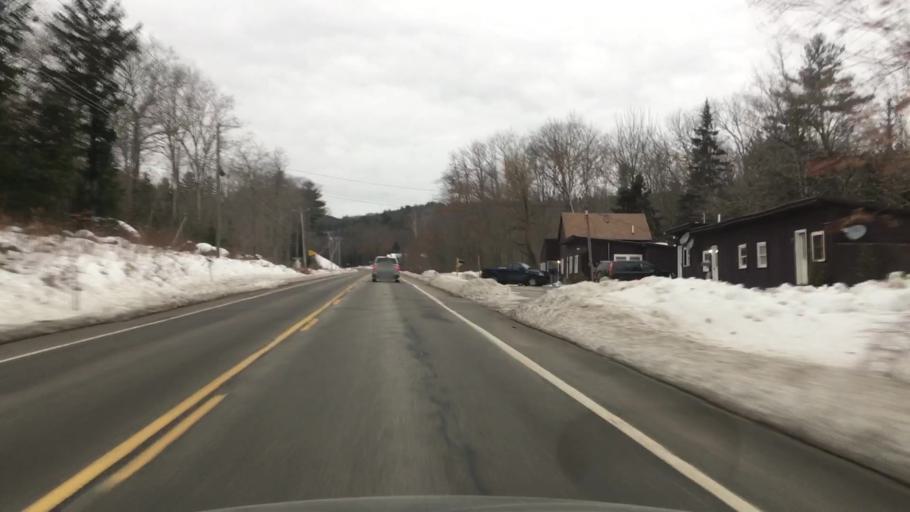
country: US
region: New Hampshire
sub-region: Merrimack County
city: Newbury
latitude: 43.3090
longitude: -72.0173
